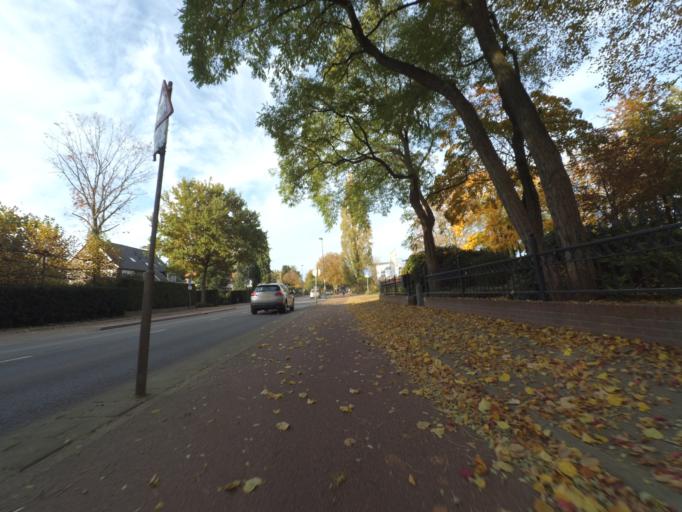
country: NL
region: Gelderland
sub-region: Gemeente Ede
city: Bennekom
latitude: 52.0094
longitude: 5.6736
